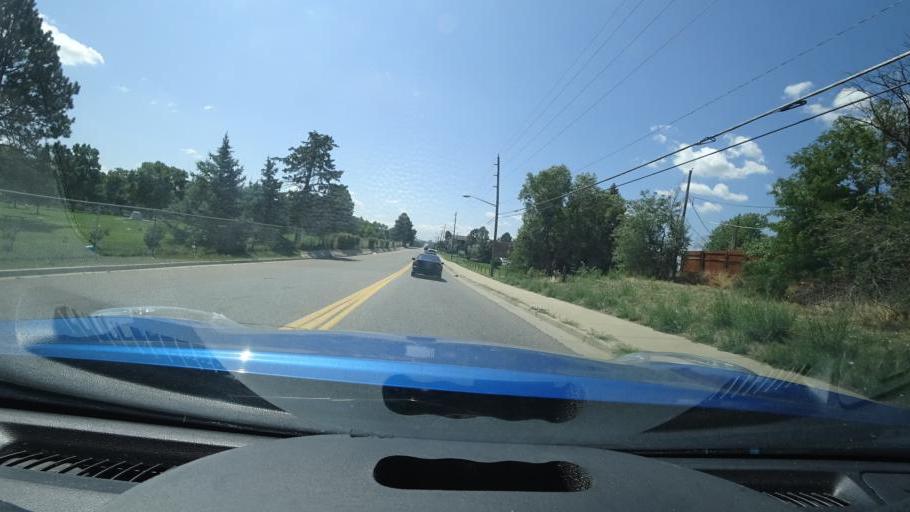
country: US
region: Colorado
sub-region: Arapahoe County
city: Glendale
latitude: 39.7029
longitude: -104.9035
